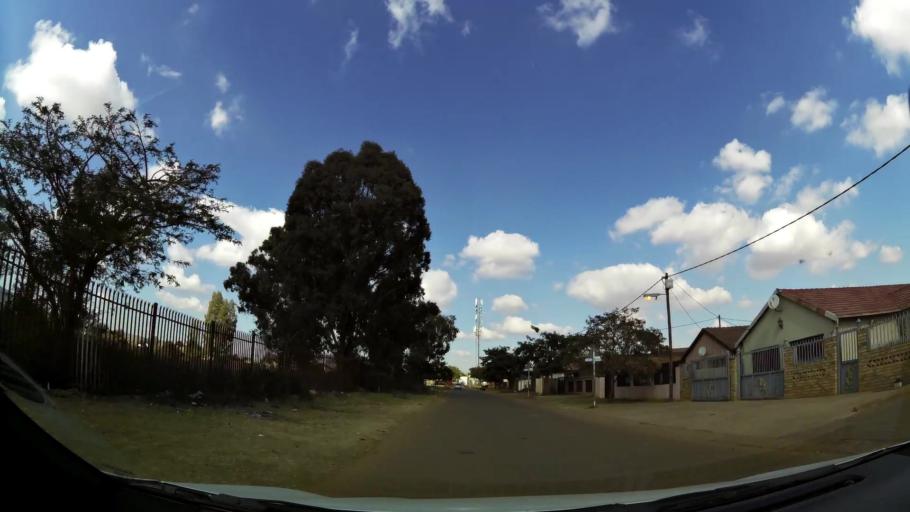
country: ZA
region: Gauteng
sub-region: City of Tshwane Metropolitan Municipality
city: Cullinan
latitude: -25.7041
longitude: 28.4109
